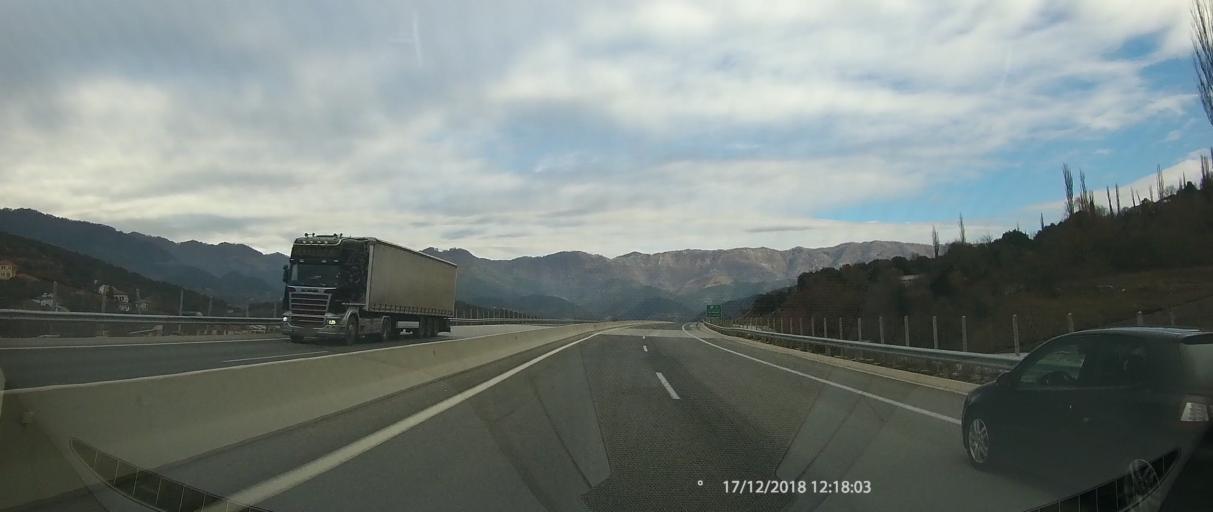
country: GR
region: Epirus
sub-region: Nomos Ioanninon
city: Metsovo
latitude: 39.7483
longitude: 21.0749
